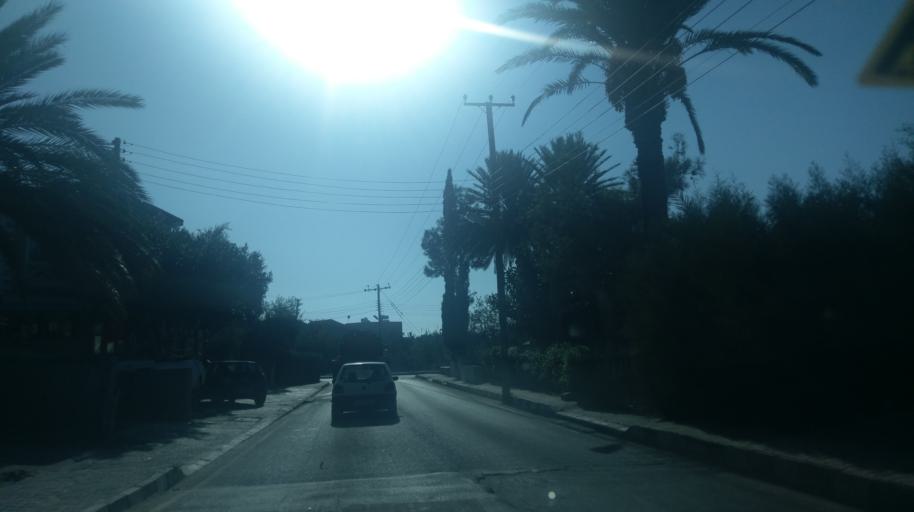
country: CY
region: Keryneia
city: Kyrenia
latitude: 35.2685
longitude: 33.3193
